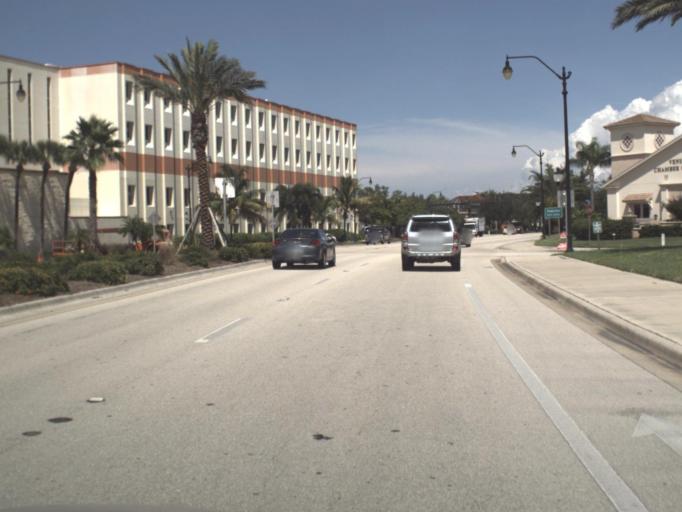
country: US
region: Florida
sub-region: Sarasota County
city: Venice
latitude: 27.0902
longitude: -82.4440
